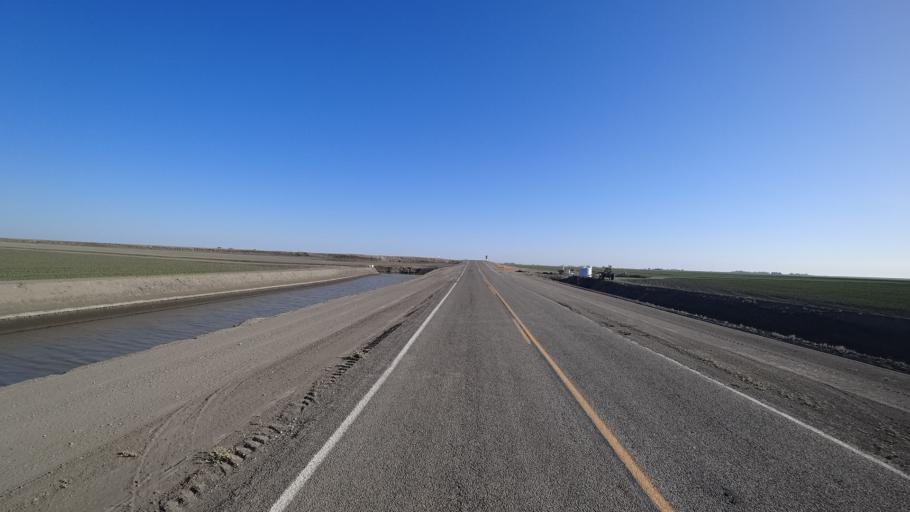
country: US
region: California
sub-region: Kings County
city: Stratford
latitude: 36.1366
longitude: -119.7981
